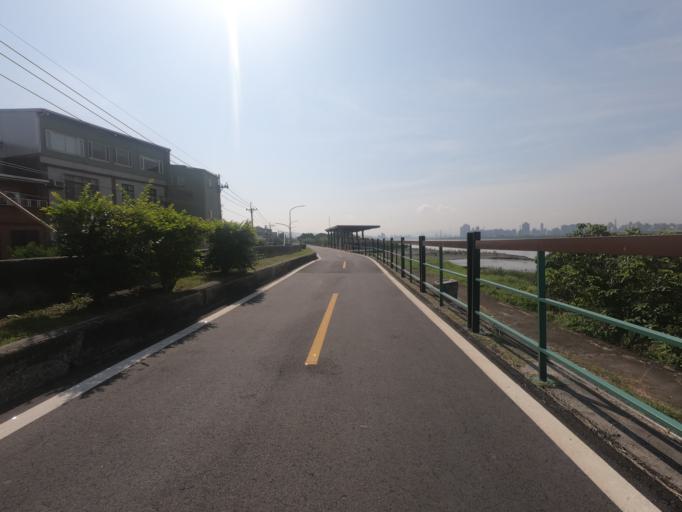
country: TW
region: Taipei
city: Taipei
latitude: 25.1063
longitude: 121.4723
